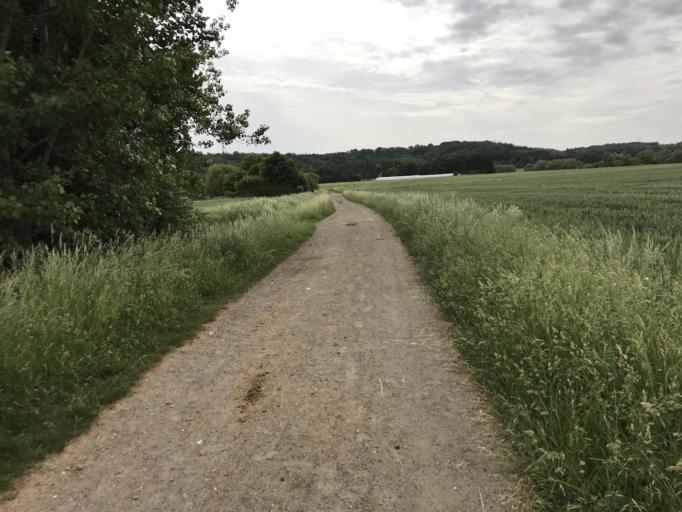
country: FR
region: Ile-de-France
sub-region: Departement de l'Essonne
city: Saulx-les-Chartreux
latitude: 48.6827
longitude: 2.2727
